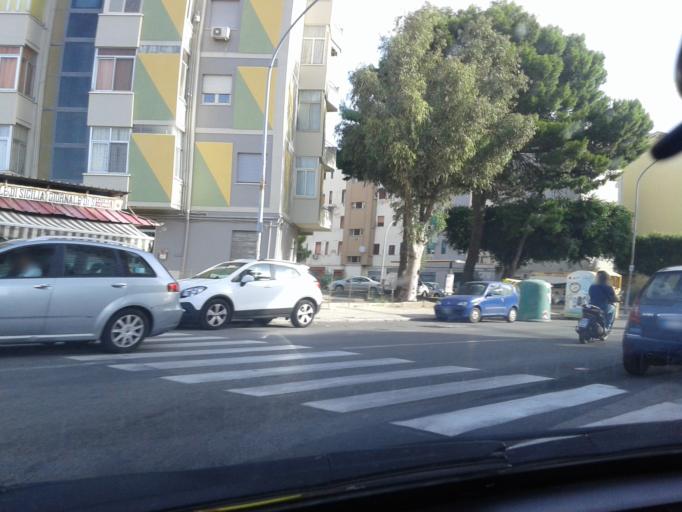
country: IT
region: Sicily
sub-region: Palermo
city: Palermo
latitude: 38.0982
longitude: 13.3341
